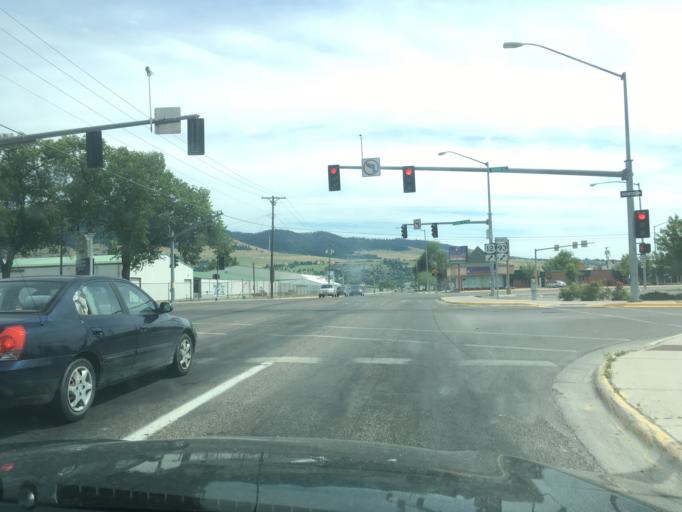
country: US
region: Montana
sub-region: Missoula County
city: Orchard Homes
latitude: 46.8500
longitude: -114.0184
